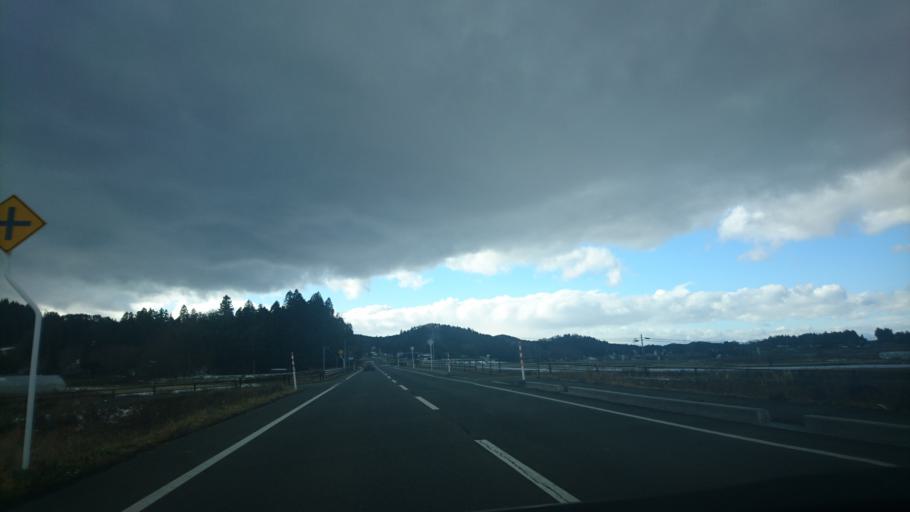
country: JP
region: Iwate
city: Mizusawa
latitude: 39.1726
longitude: 141.2619
